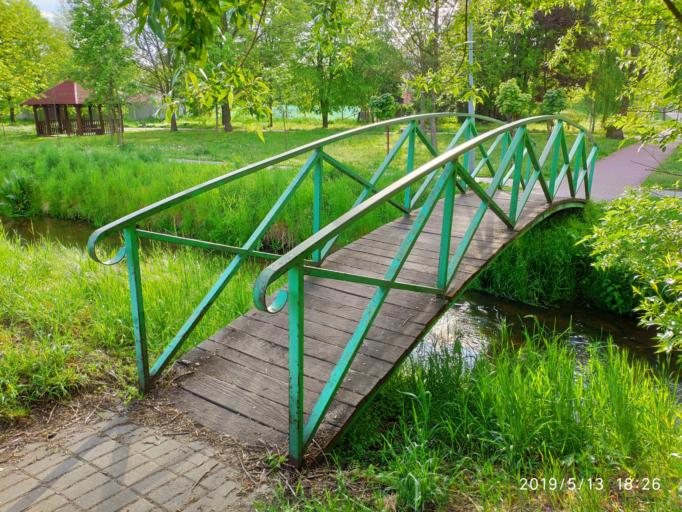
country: PL
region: Lubusz
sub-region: Powiat zielonogorski
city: Czerwiensk
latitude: 52.0121
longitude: 15.4252
